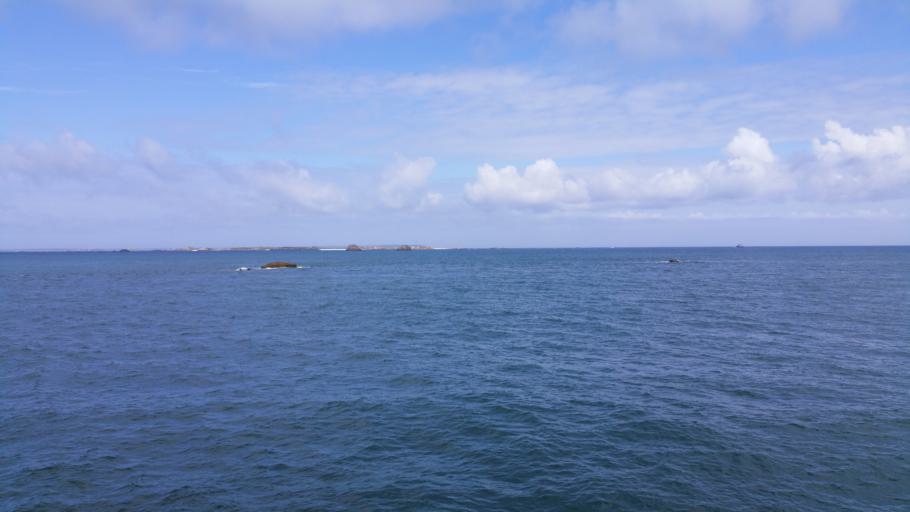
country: FR
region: Brittany
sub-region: Departement du Finistere
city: Le Conquet
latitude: 48.4024
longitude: -4.9566
